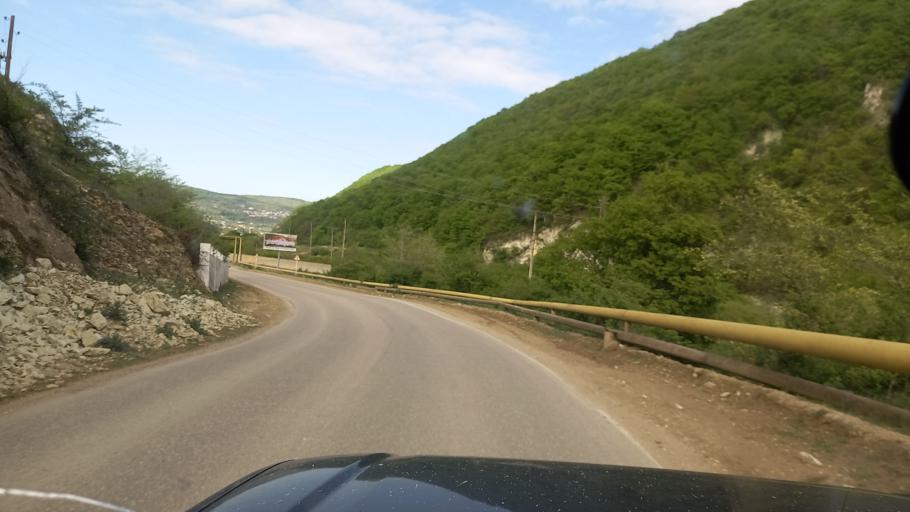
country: RU
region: Dagestan
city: Khuchni
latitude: 41.9642
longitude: 47.9585
